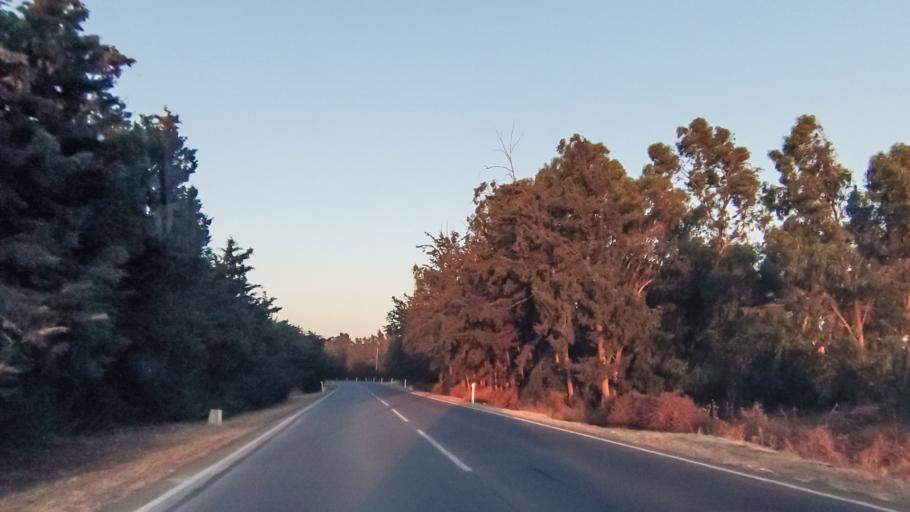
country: CY
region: Larnaka
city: Kolossi
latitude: 34.6559
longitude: 32.9237
